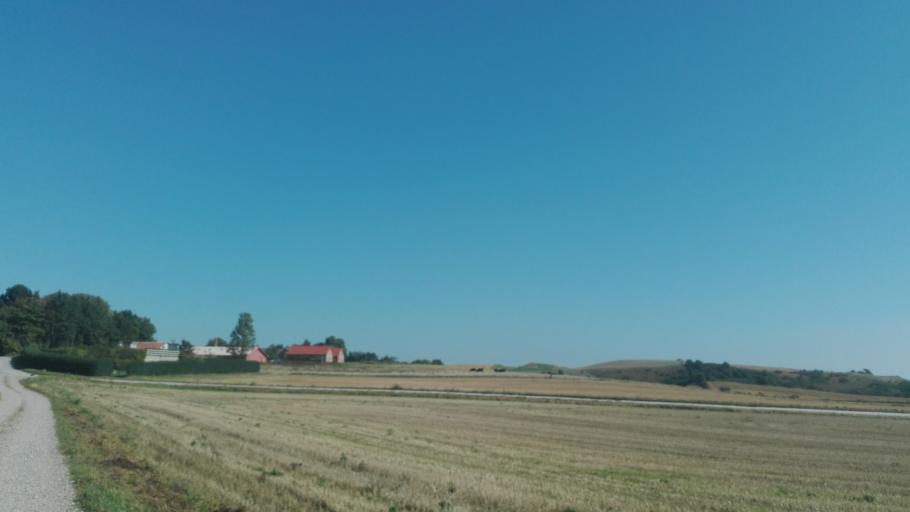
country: DK
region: Central Jutland
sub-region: Syddjurs Kommune
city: Ebeltoft
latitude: 56.2370
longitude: 10.7478
